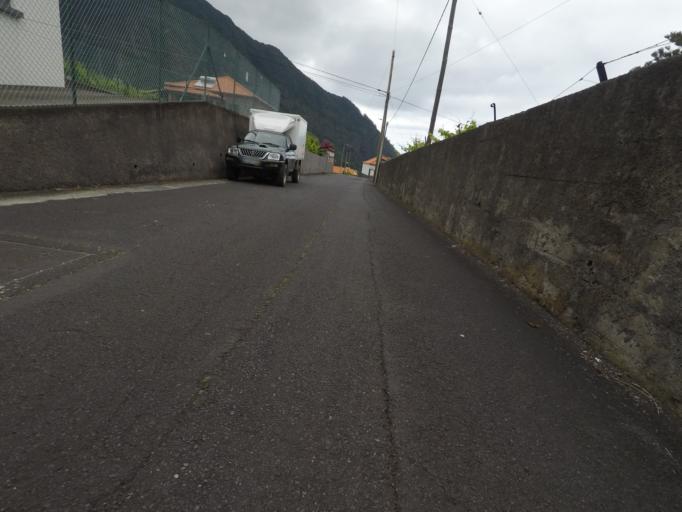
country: PT
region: Madeira
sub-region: Sao Vicente
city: Sao Vicente
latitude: 32.7899
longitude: -17.0367
